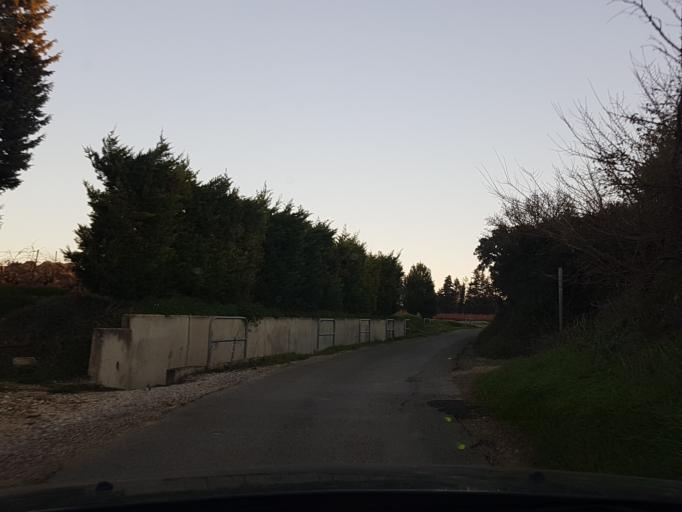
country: FR
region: Provence-Alpes-Cote d'Azur
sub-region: Departement du Vaucluse
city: Vedene
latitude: 43.9635
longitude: 4.9098
